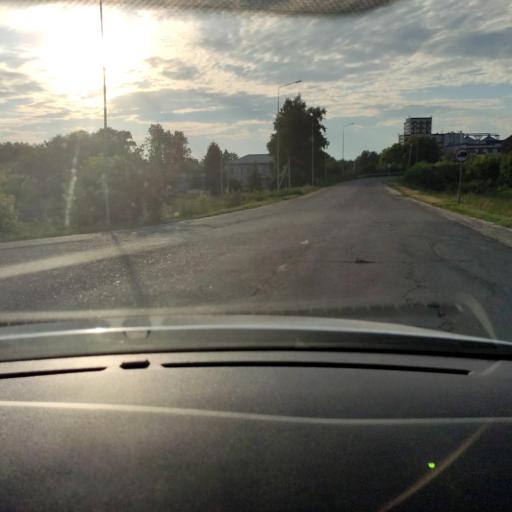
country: RU
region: Tatarstan
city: Vysokaya Gora
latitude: 55.9776
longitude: 49.3072
